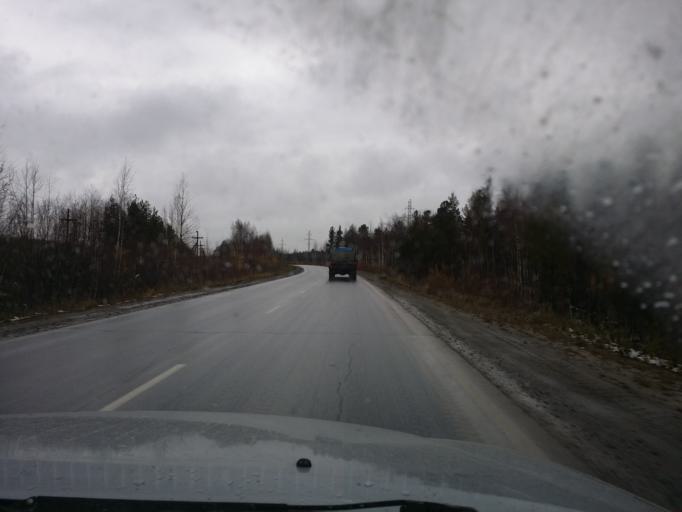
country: RU
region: Khanty-Mansiyskiy Avtonomnyy Okrug
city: Megion
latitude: 61.1423
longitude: 75.7594
